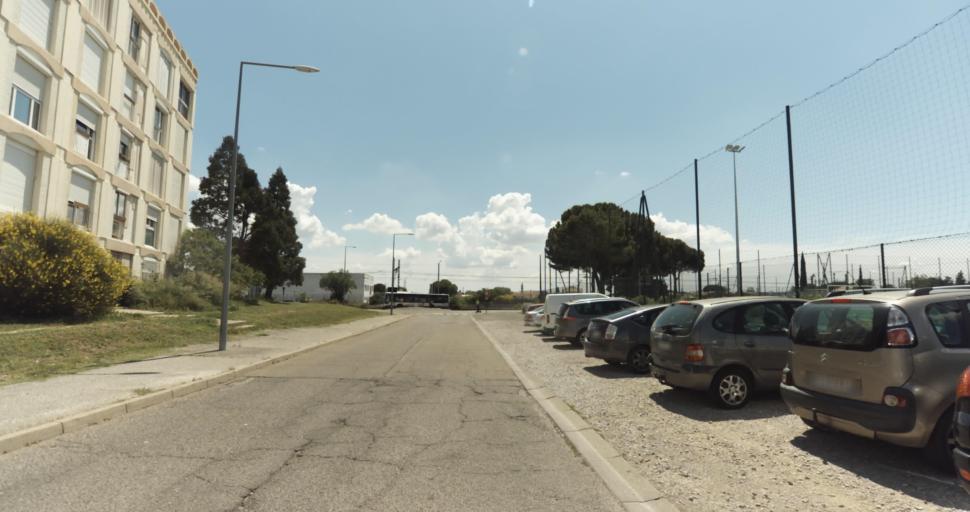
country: FR
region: Languedoc-Roussillon
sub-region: Departement du Gard
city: Nimes
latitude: 43.8167
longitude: 4.3317
